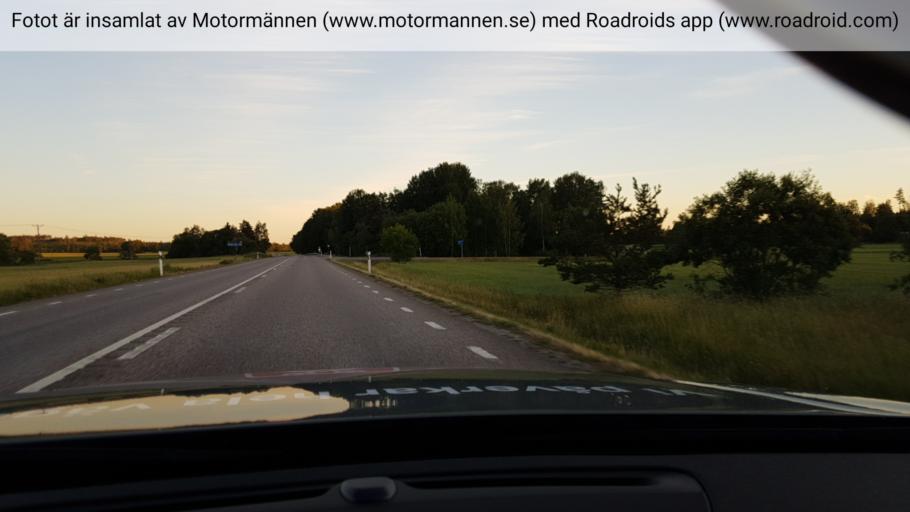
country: SE
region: Vaestmanland
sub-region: Hallstahammars Kommun
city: Kolback
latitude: 59.5512
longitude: 16.3357
